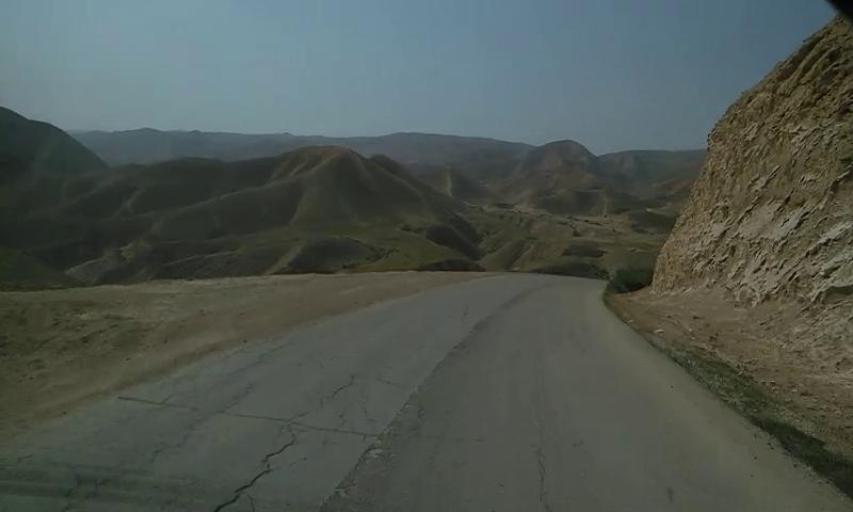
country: PS
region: West Bank
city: Jericho
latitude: 31.7800
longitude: 35.4203
